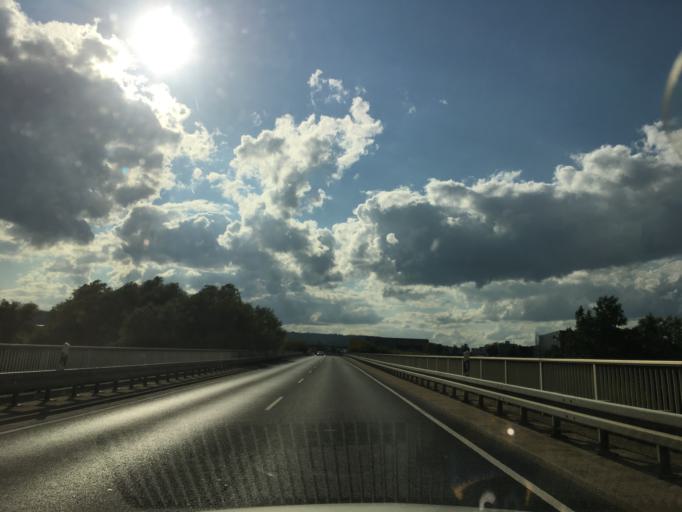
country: DE
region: Hesse
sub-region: Regierungsbezirk Darmstadt
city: Neu-Anspach
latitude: 50.3055
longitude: 8.5240
